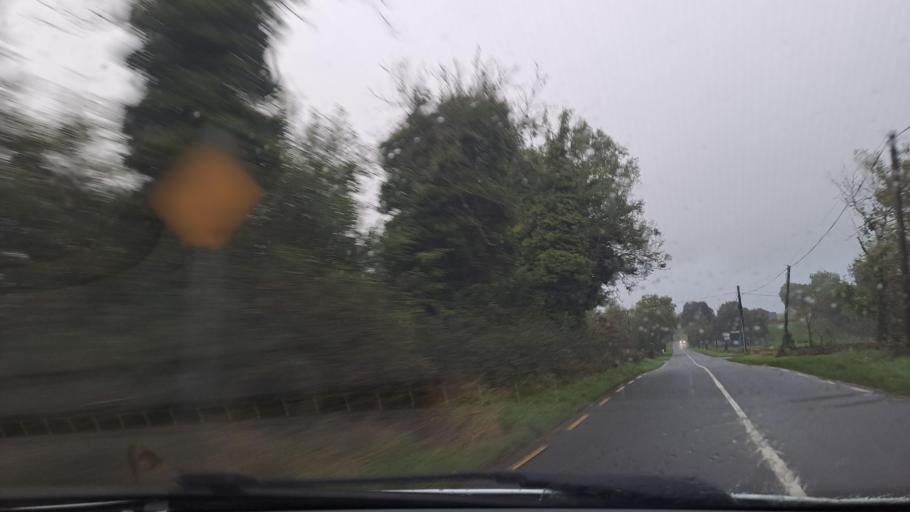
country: IE
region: Ulster
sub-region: County Monaghan
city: Carrickmacross
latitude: 53.9875
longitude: -6.6966
